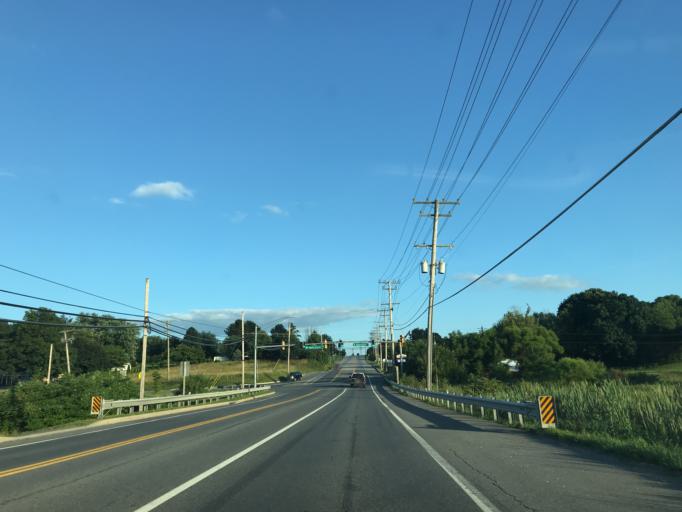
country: US
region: Maryland
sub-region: Carroll County
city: Manchester
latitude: 39.6520
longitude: -76.8798
